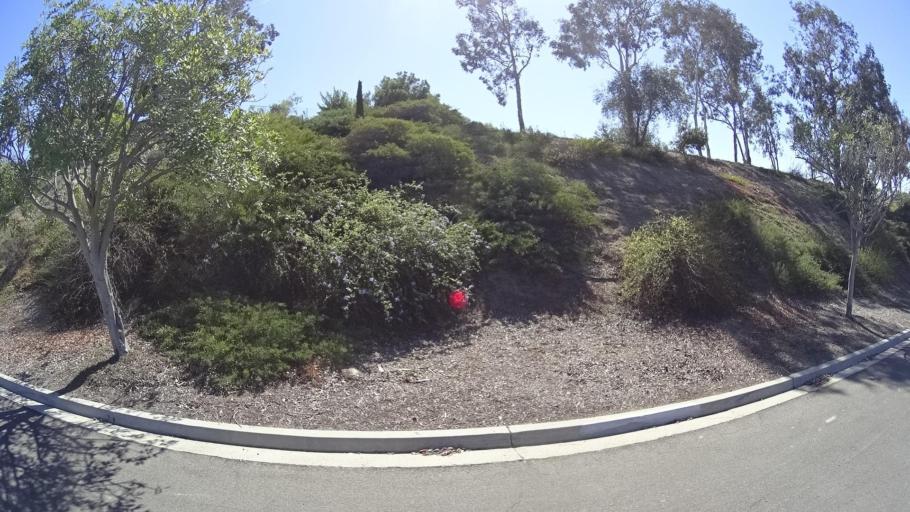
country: US
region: California
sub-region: San Diego County
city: Bonita
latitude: 32.6704
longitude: -117.0080
